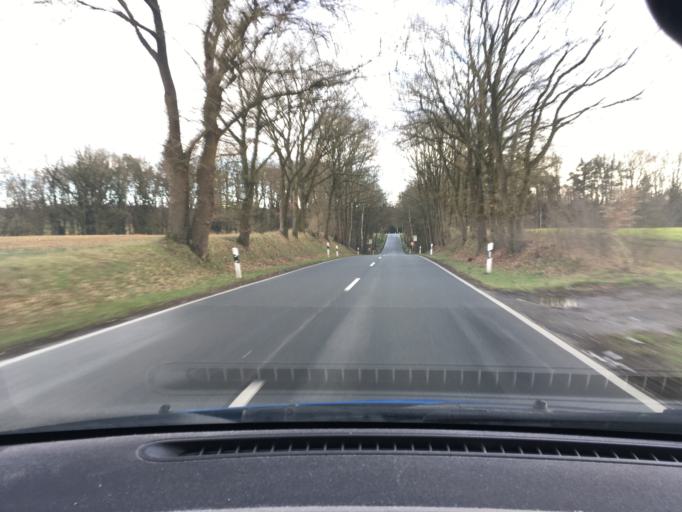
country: DE
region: Lower Saxony
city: Hanstedt
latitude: 53.2309
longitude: 10.0226
